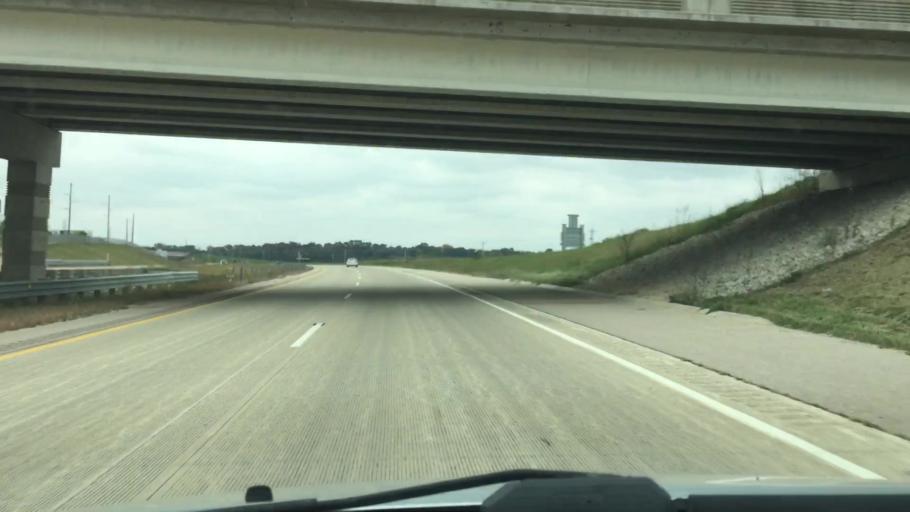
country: US
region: Wisconsin
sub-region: Rock County
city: Milton
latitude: 42.7615
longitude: -88.9363
